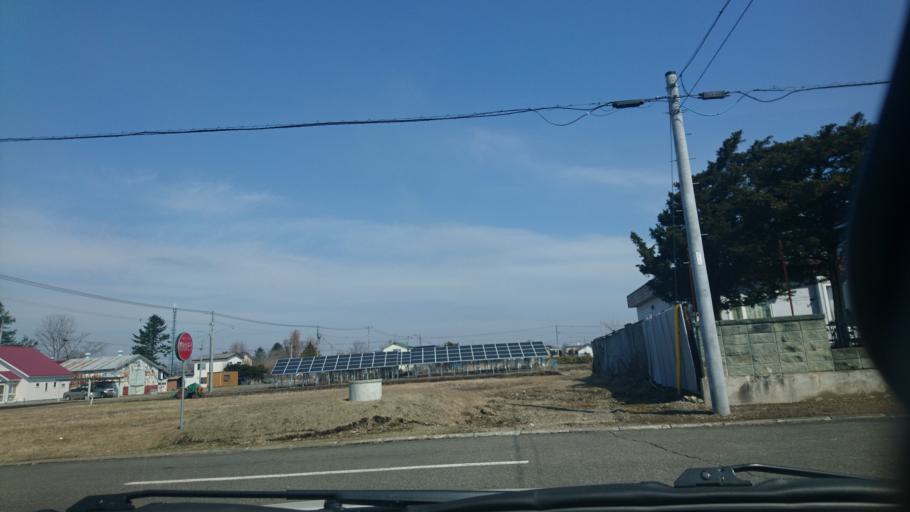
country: JP
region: Hokkaido
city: Otofuke
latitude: 43.0946
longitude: 143.2276
